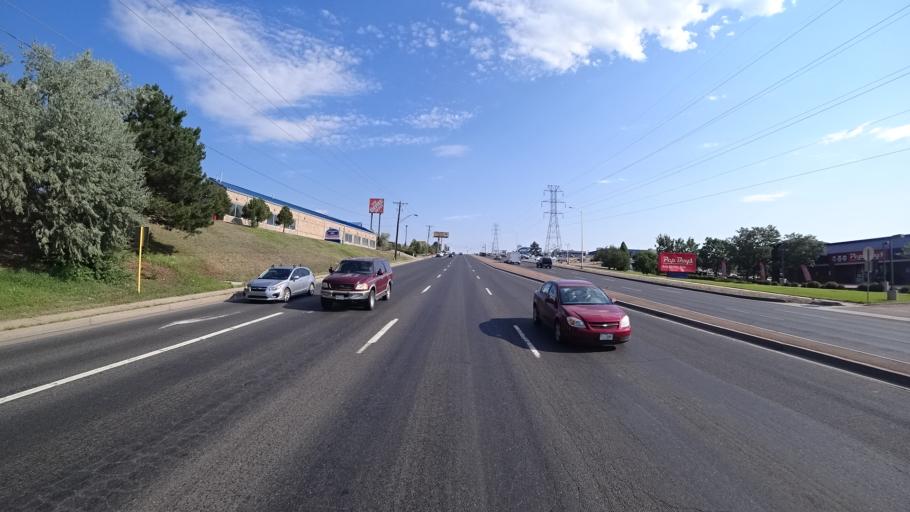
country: US
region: Colorado
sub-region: El Paso County
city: Stratmoor
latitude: 38.8329
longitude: -104.7575
